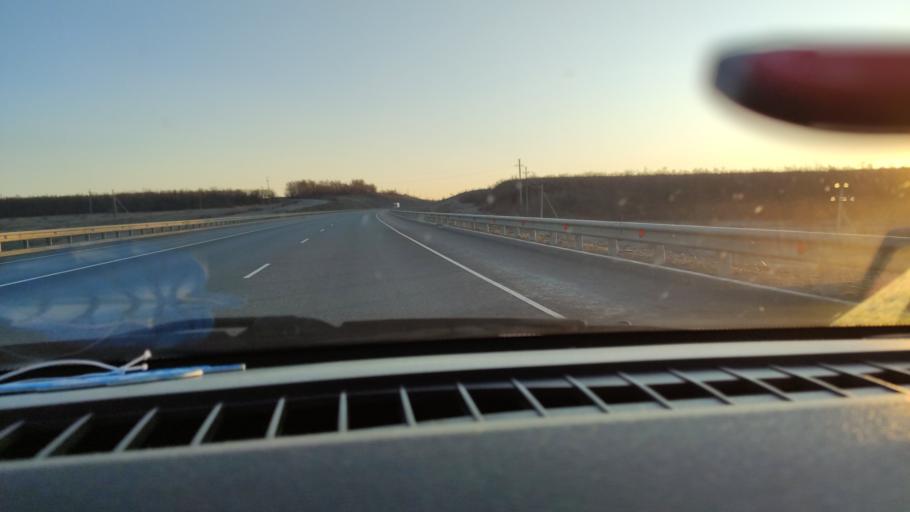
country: RU
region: Saratov
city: Yelshanka
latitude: 51.8810
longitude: 46.5105
